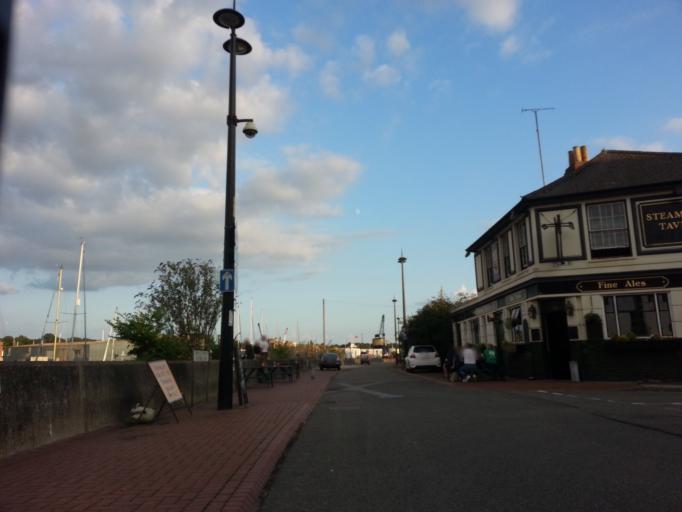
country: GB
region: England
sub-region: Suffolk
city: Ipswich
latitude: 52.0493
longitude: 1.1590
